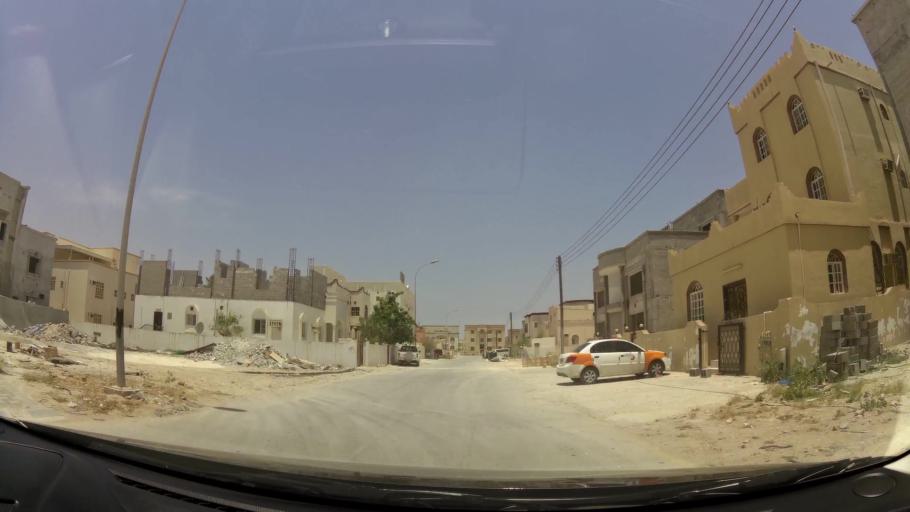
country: OM
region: Zufar
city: Salalah
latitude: 17.0807
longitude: 54.1623
